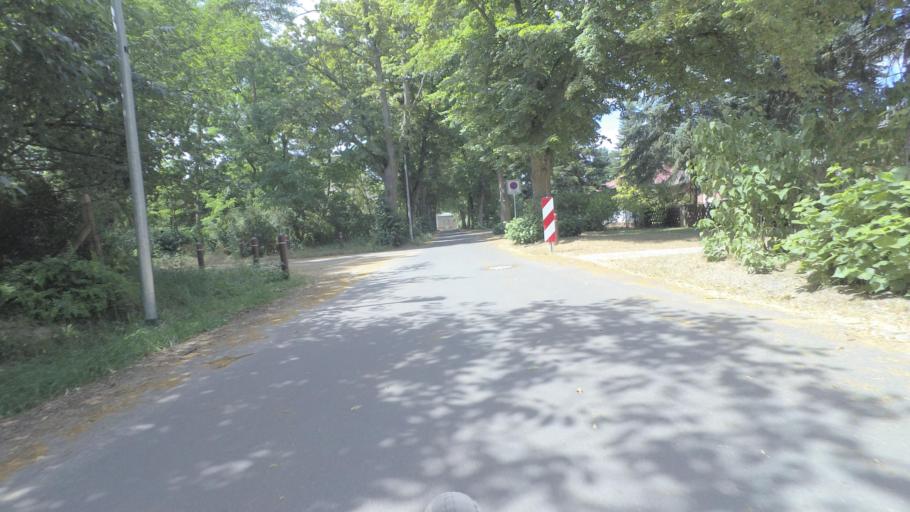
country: DE
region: Brandenburg
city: Teltow
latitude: 52.3689
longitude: 13.2610
